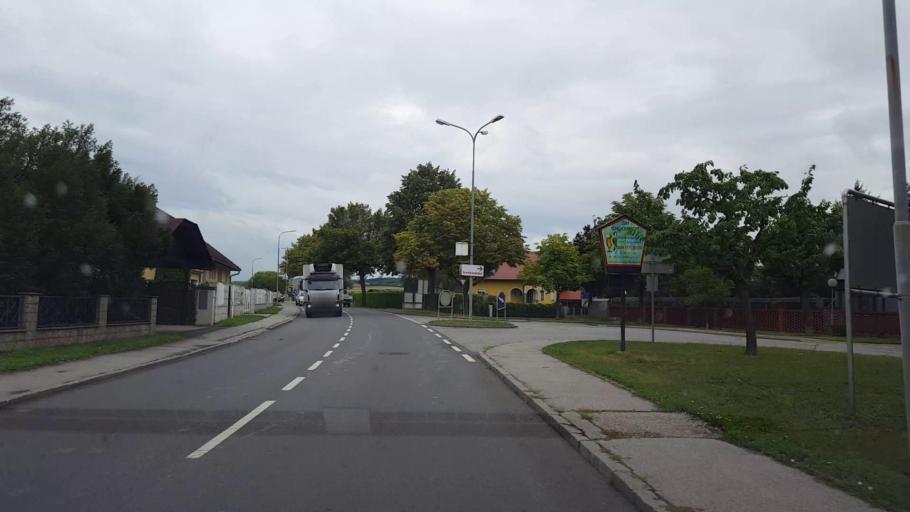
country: AT
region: Lower Austria
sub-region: Politischer Bezirk Wien-Umgebung
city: Schwadorf
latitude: 48.0698
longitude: 16.5765
